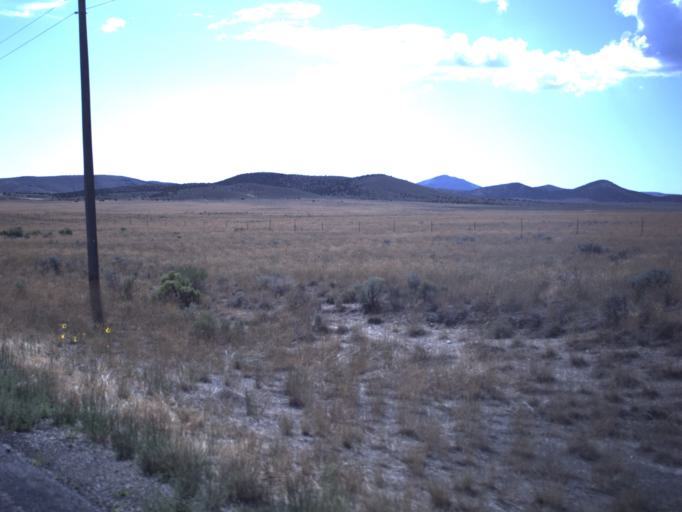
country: US
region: Utah
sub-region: Tooele County
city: Tooele
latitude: 40.0843
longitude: -112.4186
